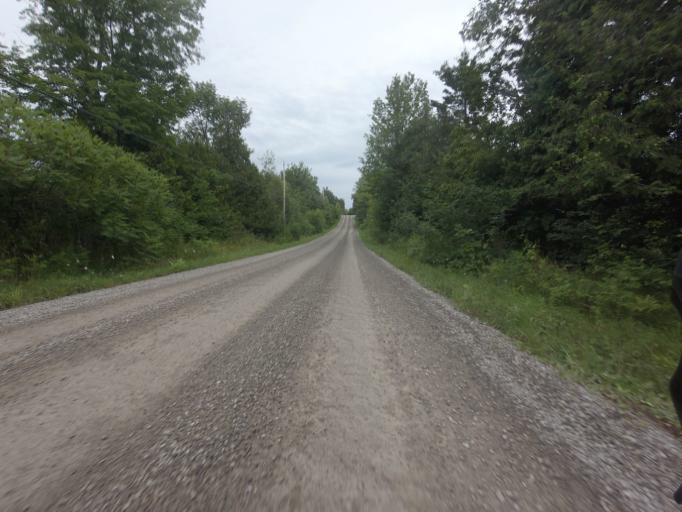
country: CA
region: Ontario
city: Carleton Place
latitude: 45.1476
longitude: -76.2293
